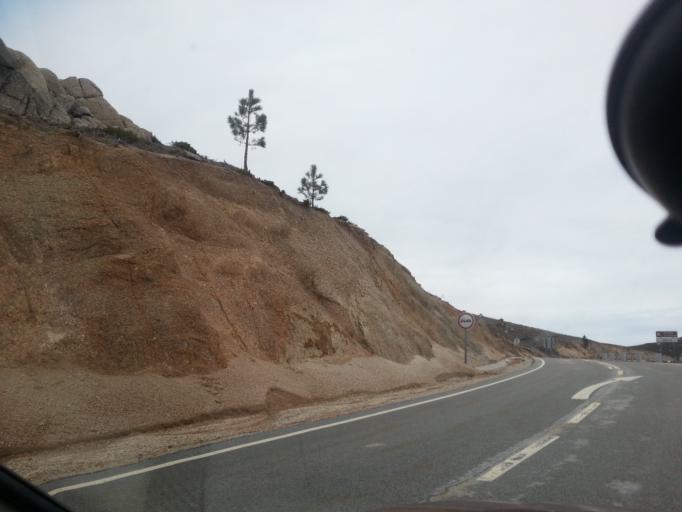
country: PT
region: Guarda
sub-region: Seia
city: Seia
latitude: 40.3455
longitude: -7.6934
